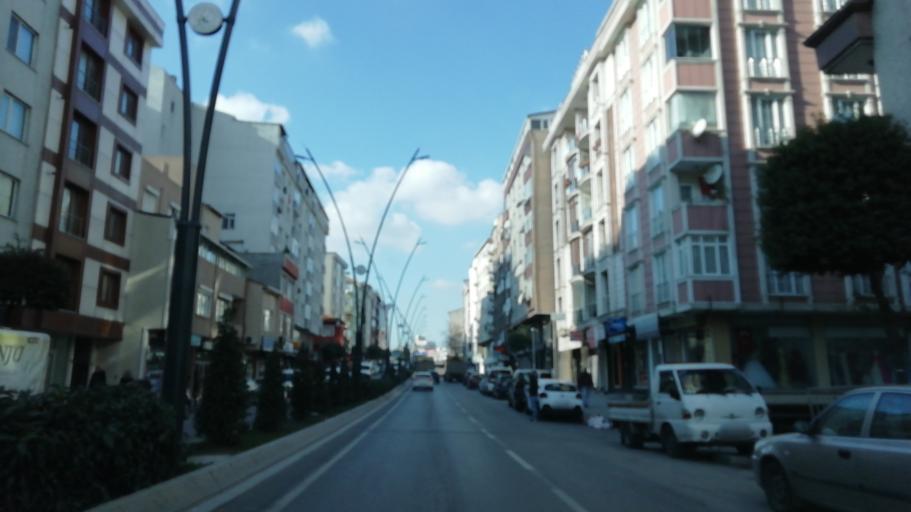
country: TR
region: Istanbul
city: Esenler
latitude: 41.0579
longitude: 28.9202
